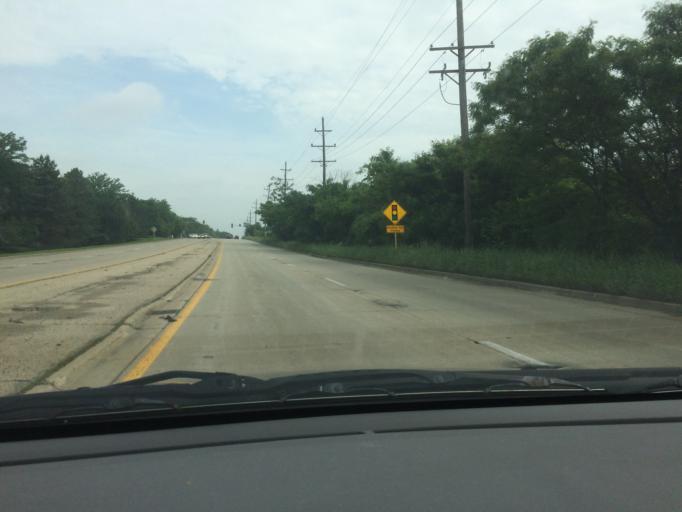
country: US
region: Illinois
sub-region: DuPage County
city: Wayne
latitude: 41.9552
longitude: -88.2051
